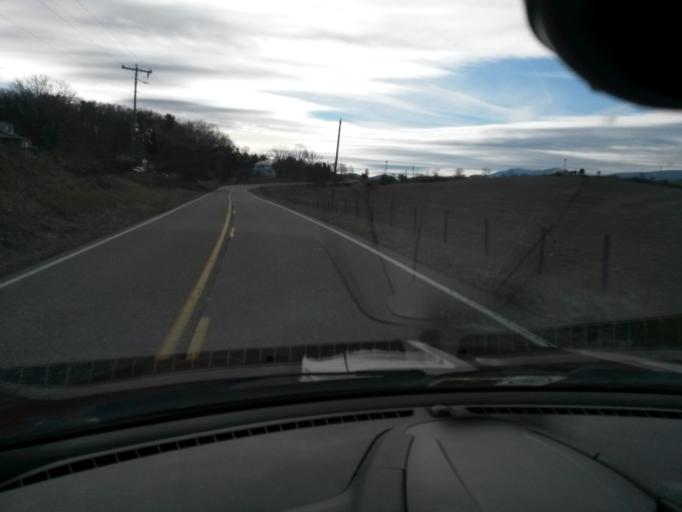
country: US
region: Virginia
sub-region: City of Staunton
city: Staunton
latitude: 38.2612
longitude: -79.1560
